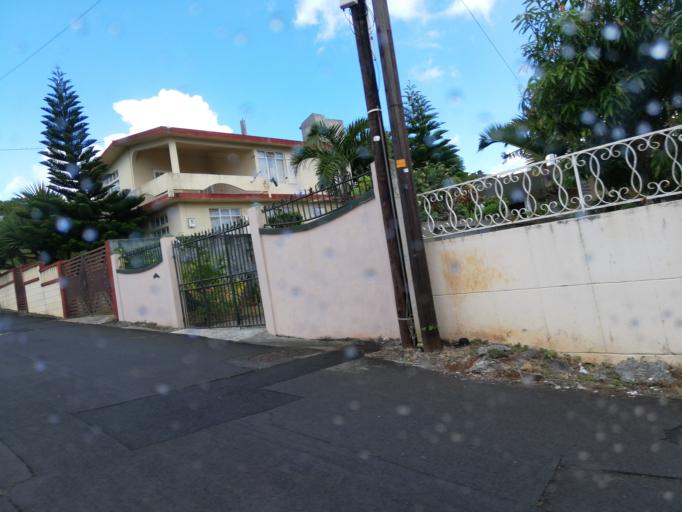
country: MU
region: Moka
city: Moka
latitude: -20.2132
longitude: 57.4738
